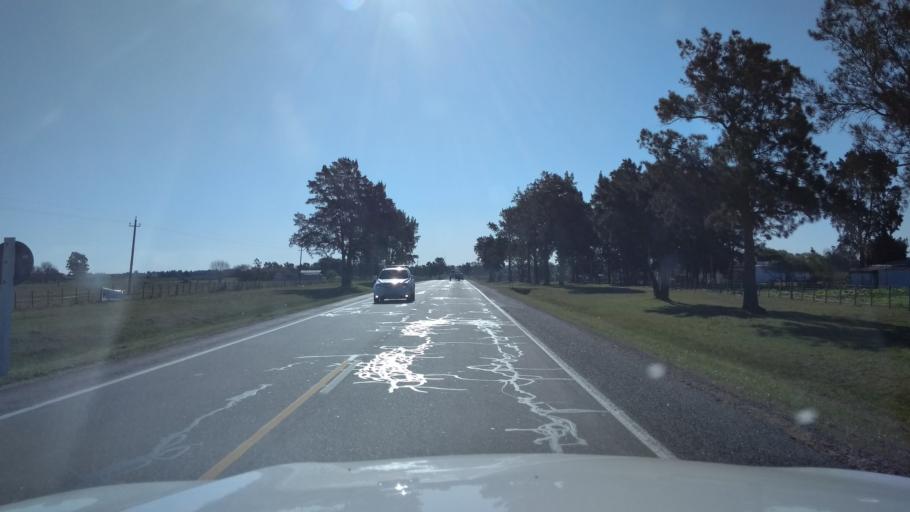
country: UY
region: Canelones
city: San Jacinto
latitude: -34.5761
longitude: -55.8480
